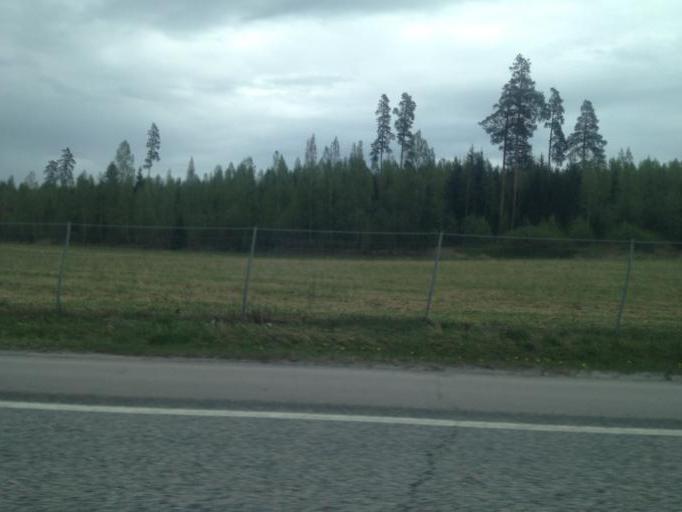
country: FI
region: Uusimaa
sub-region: Helsinki
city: Nurmijaervi
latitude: 60.4237
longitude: 24.8258
